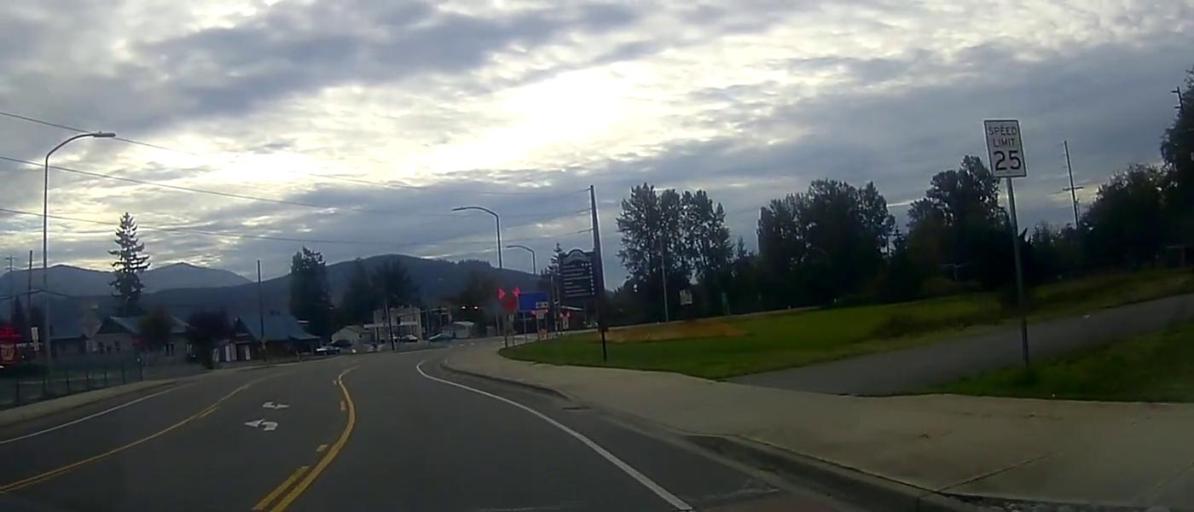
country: US
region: Washington
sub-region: Skagit County
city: Sedro-Woolley
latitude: 48.5069
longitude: -122.2463
